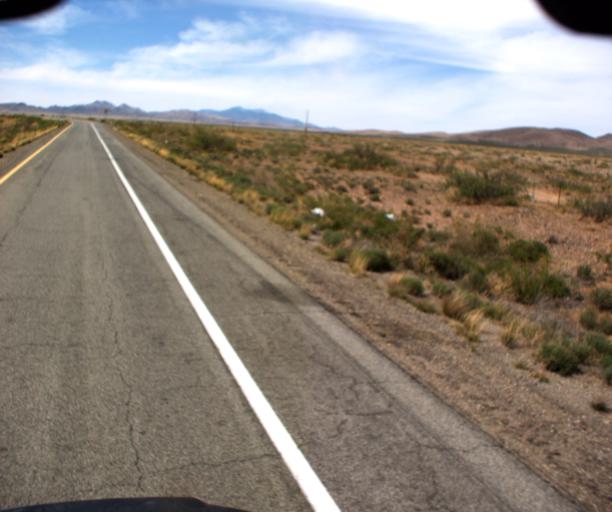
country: US
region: Arizona
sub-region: Cochise County
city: Willcox
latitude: 32.3615
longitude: -109.6172
